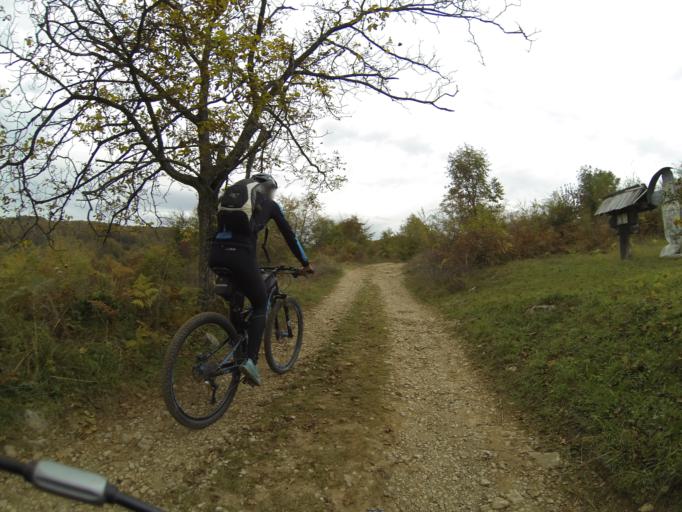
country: RO
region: Gorj
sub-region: Comuna Tismana
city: Sohodol
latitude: 45.0749
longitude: 22.8612
